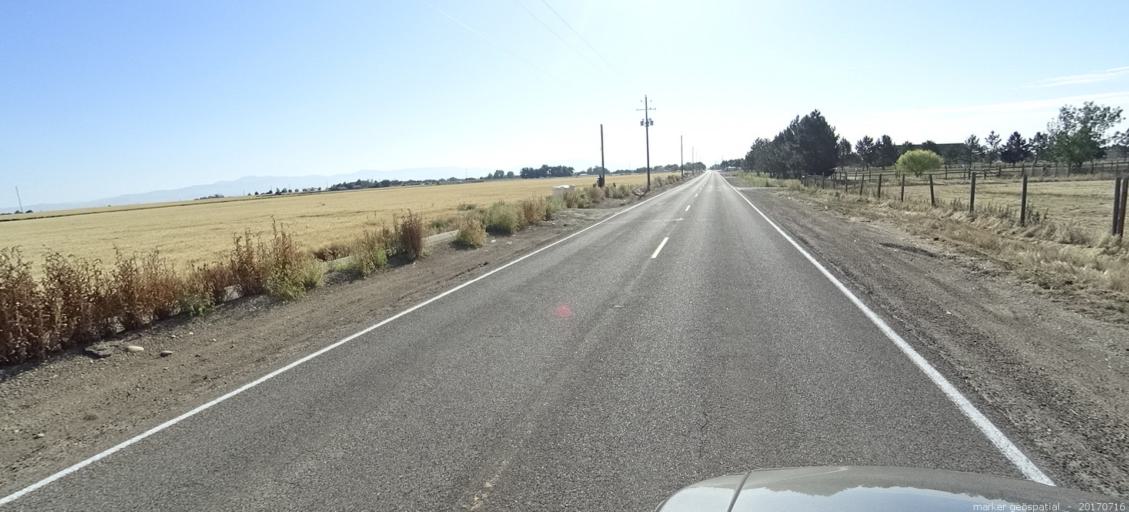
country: US
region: Idaho
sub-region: Ada County
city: Kuna
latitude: 43.5464
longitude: -116.4009
